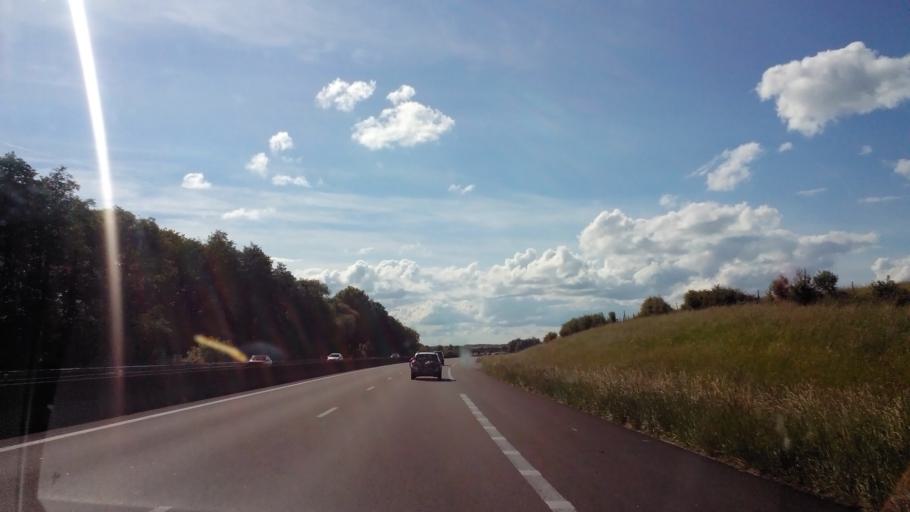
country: FR
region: Bourgogne
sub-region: Departement de la Cote-d'Or
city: Pouilly-en-Auxois
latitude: 47.1996
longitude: 4.6546
